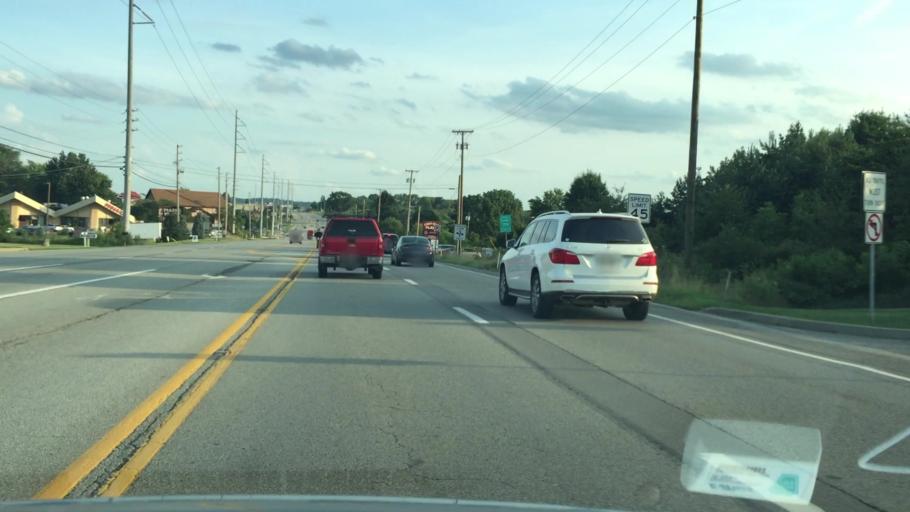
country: US
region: Pennsylvania
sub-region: Butler County
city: Cranberry Township
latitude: 40.7034
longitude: -80.1045
